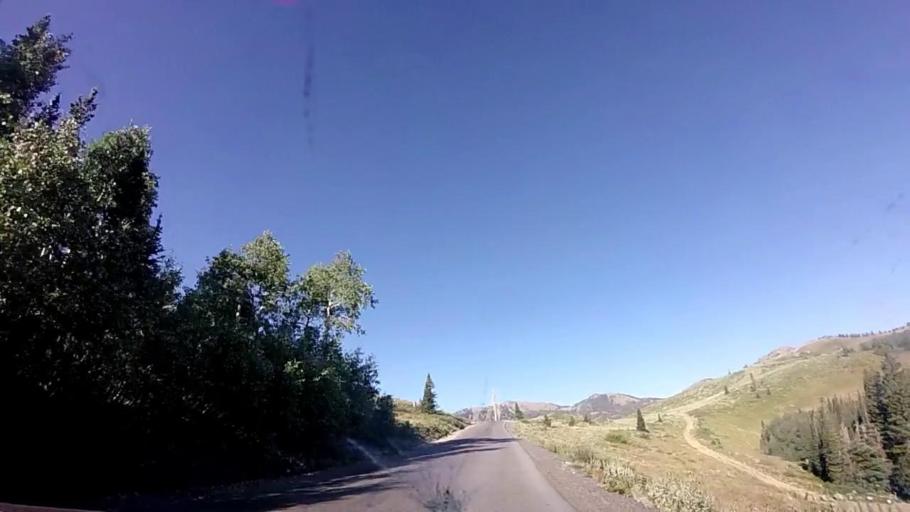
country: US
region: Utah
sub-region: Summit County
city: Park City
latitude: 40.6069
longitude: -111.5071
